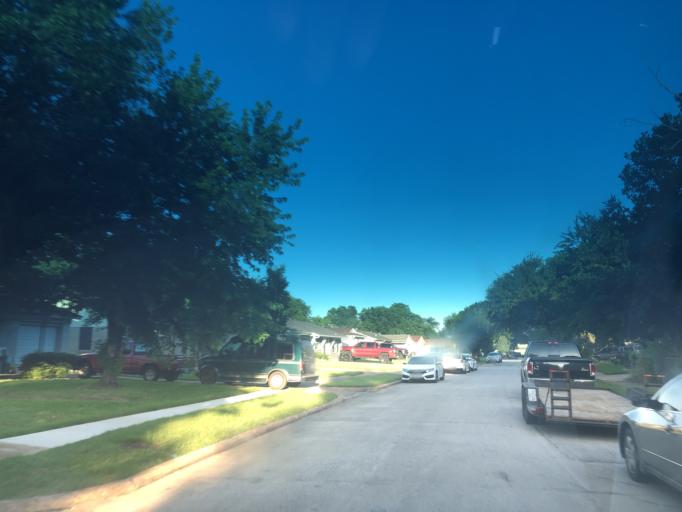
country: US
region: Texas
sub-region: Dallas County
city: Grand Prairie
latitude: 32.7051
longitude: -97.0133
